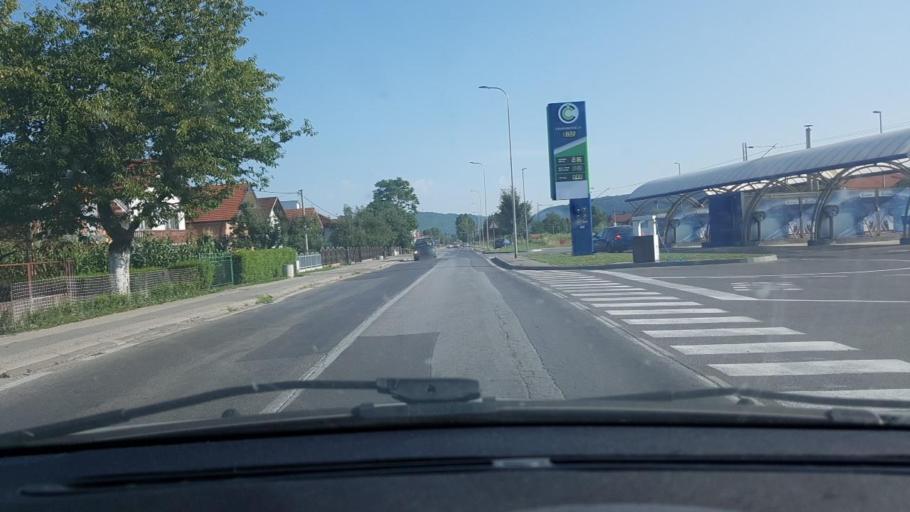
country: BA
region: Federation of Bosnia and Herzegovina
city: Bihac
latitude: 44.8296
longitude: 15.8818
